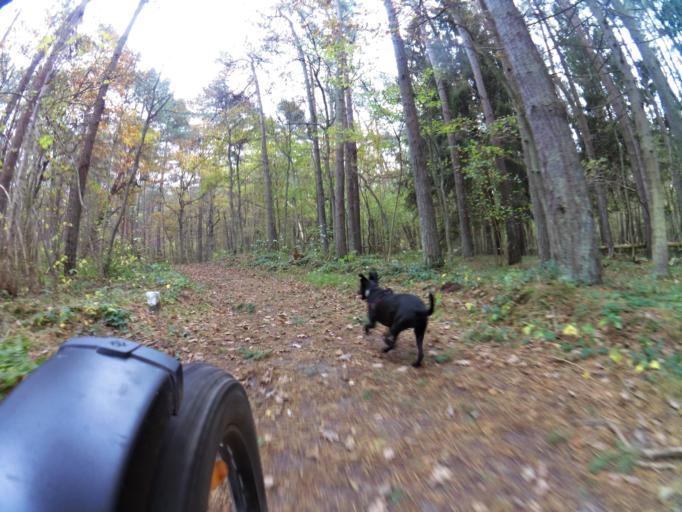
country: PL
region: Pomeranian Voivodeship
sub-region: Powiat pucki
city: Krokowa
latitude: 54.8298
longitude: 18.1175
